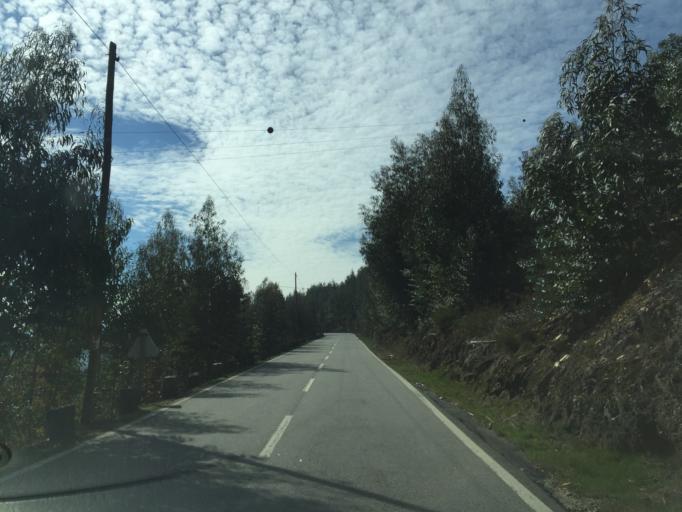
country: PT
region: Aveiro
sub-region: Arouca
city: Arouca
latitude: 40.9549
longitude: -8.1824
